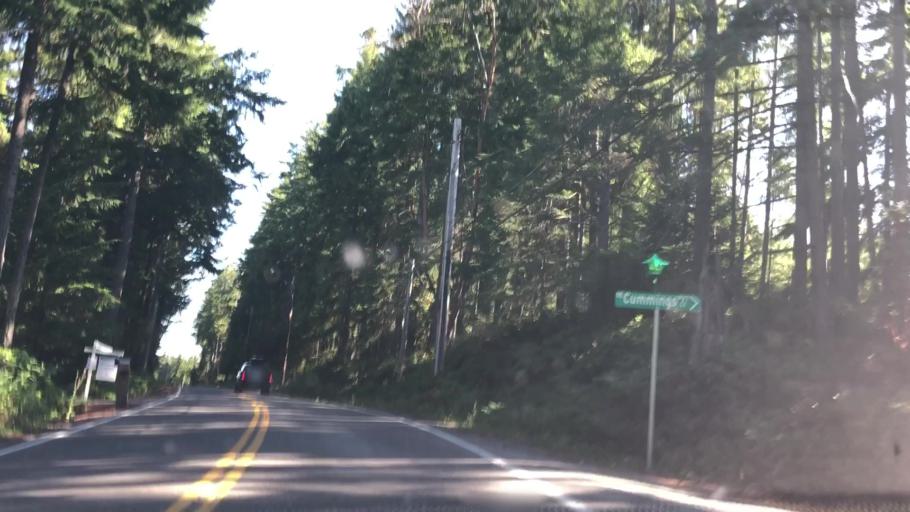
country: US
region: Washington
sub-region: Kitsap County
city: Indianola
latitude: 47.7695
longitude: -122.5151
